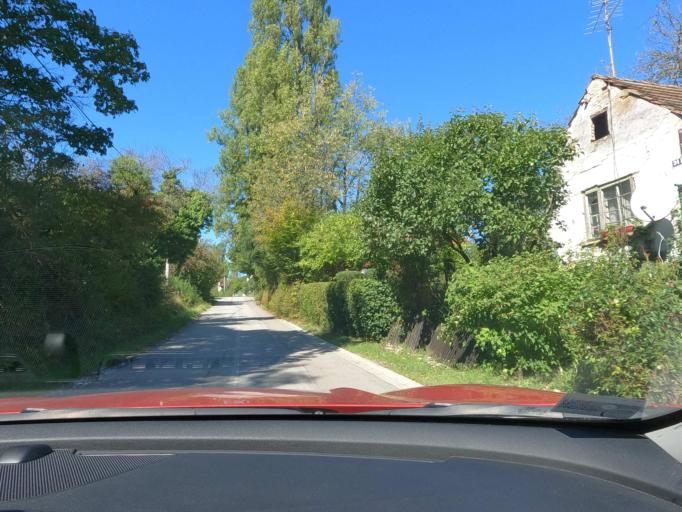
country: HR
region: Sisacko-Moslavacka
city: Petrinja
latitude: 45.4671
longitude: 16.2841
